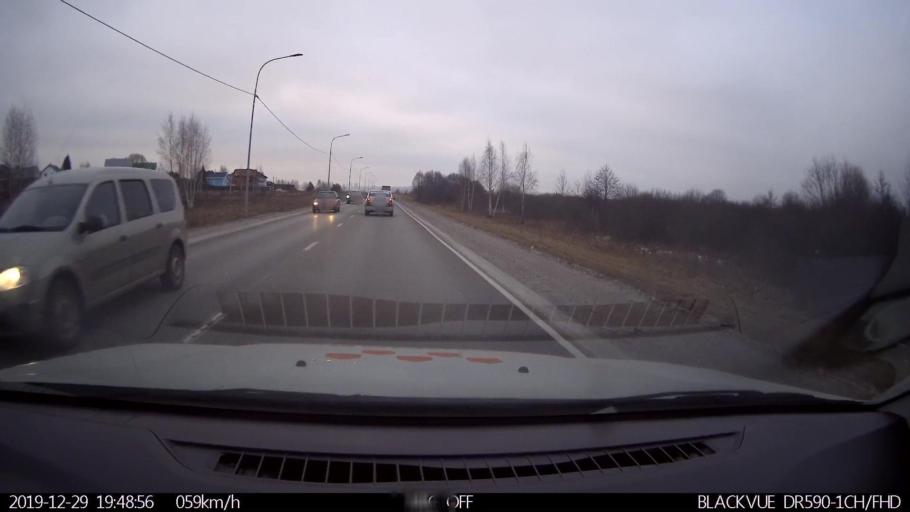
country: RU
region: Nizjnij Novgorod
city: Neklyudovo
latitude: 56.3817
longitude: 44.0104
